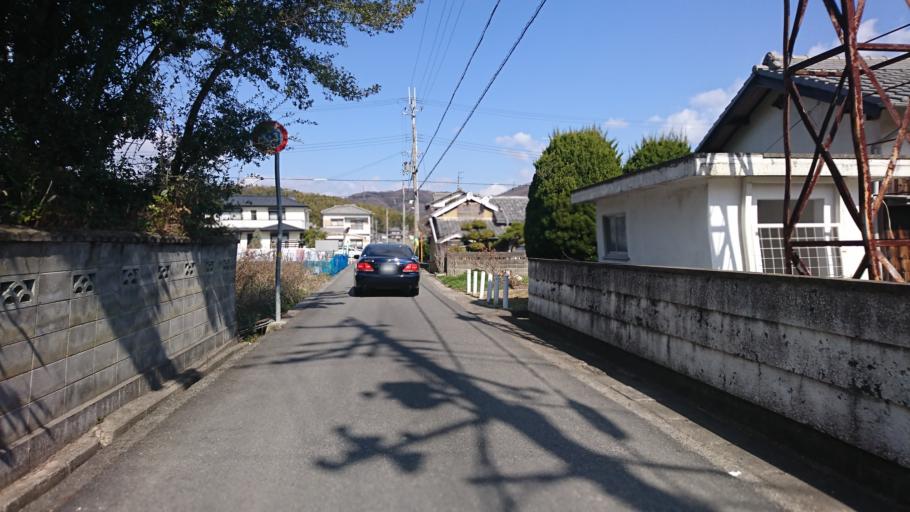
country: JP
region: Hyogo
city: Kakogawacho-honmachi
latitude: 34.8183
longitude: 134.8020
